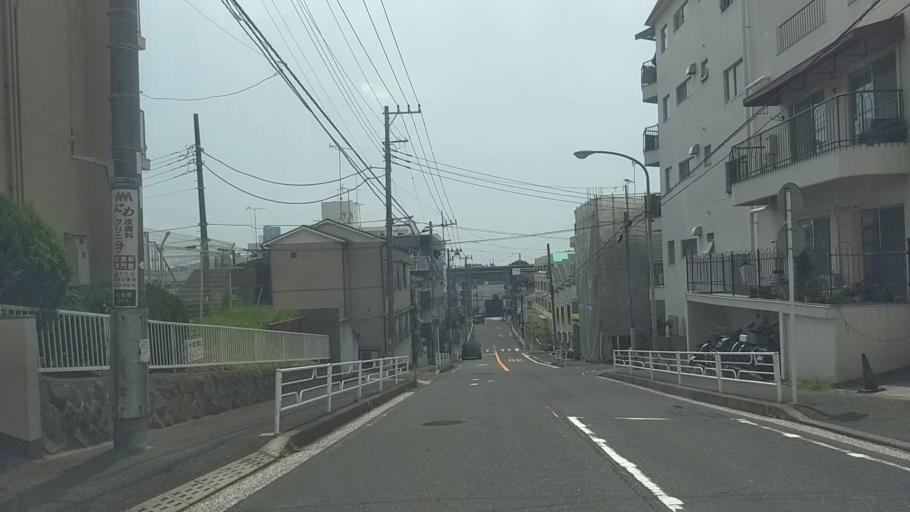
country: JP
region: Kanagawa
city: Yokohama
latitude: 35.4986
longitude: 139.6436
